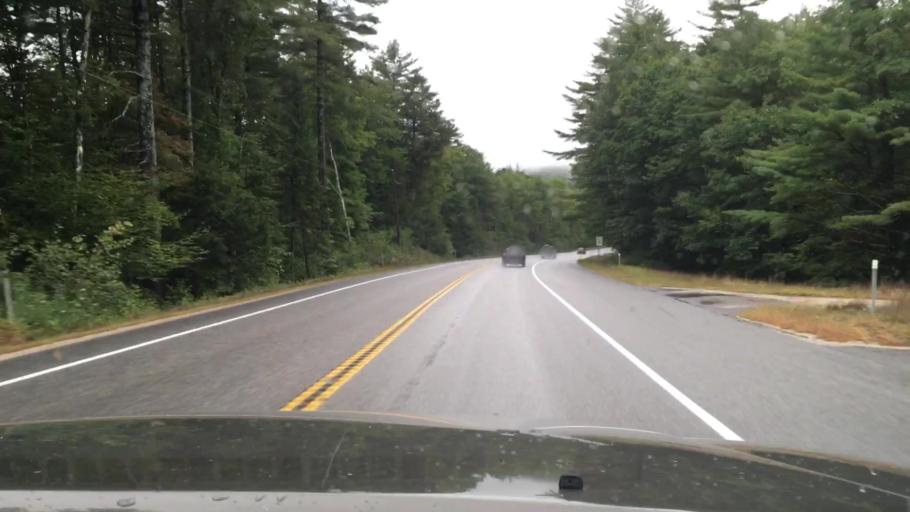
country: US
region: New Hampshire
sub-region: Hillsborough County
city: Antrim
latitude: 43.0697
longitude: -72.0342
